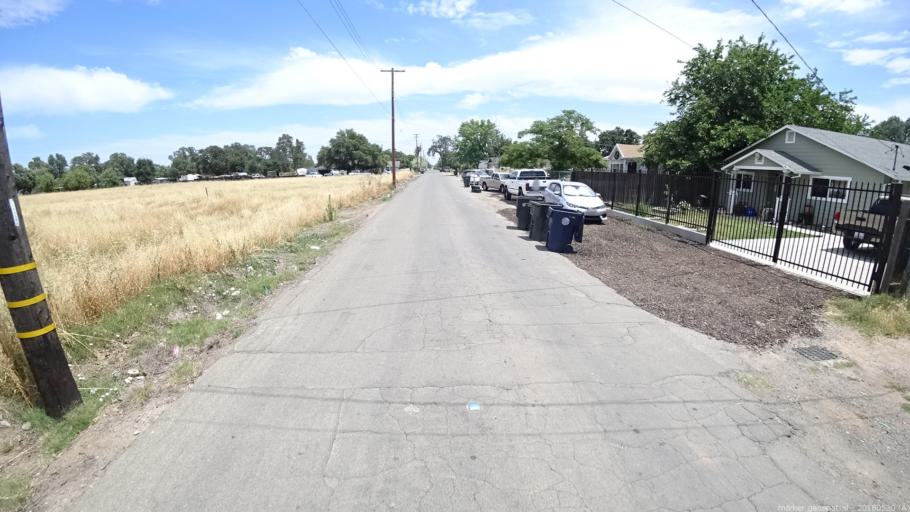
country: US
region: California
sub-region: Sacramento County
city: Sacramento
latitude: 38.6287
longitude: -121.4661
